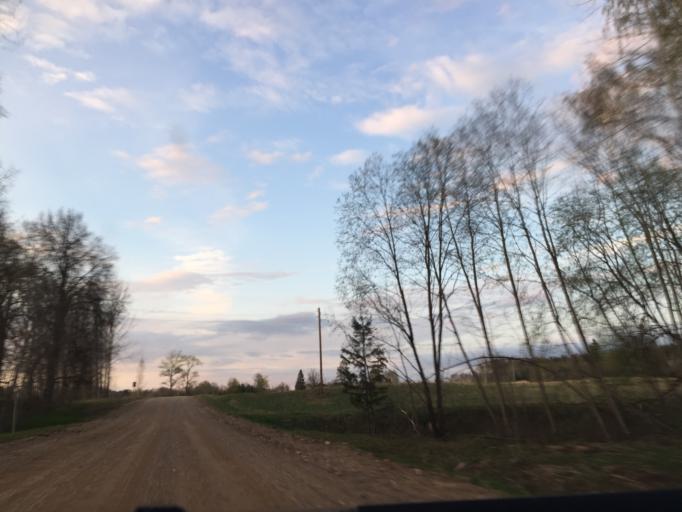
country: LV
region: Gulbenes Rajons
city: Gulbene
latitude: 57.2583
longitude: 26.9199
